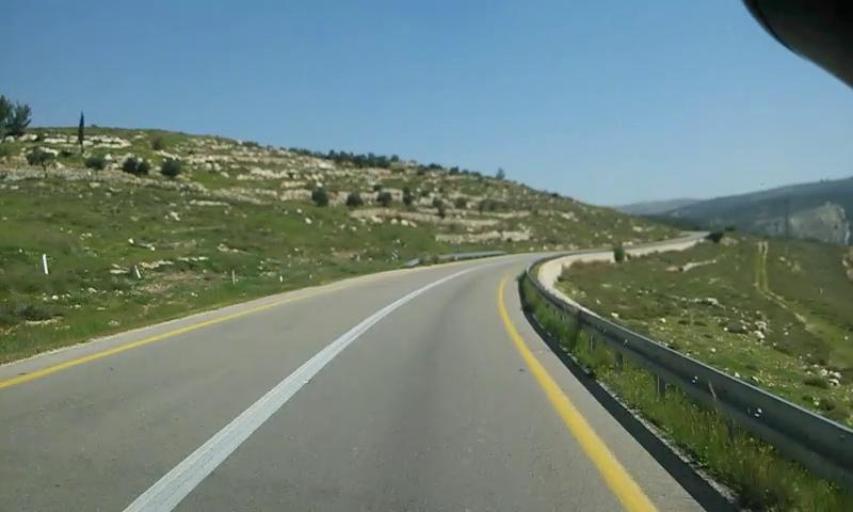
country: PS
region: West Bank
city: Surif
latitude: 31.6727
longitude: 35.0847
